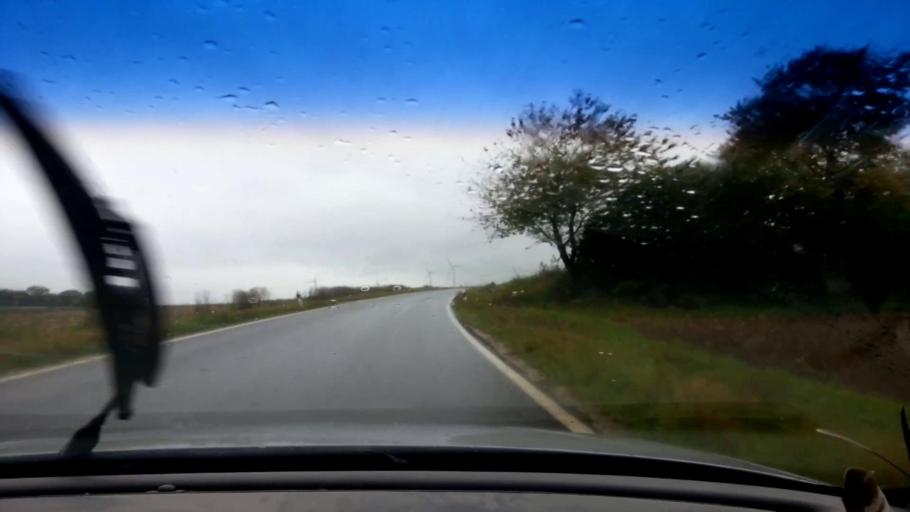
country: DE
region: Bavaria
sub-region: Upper Franconia
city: Poxdorf
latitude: 49.9361
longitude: 11.1282
